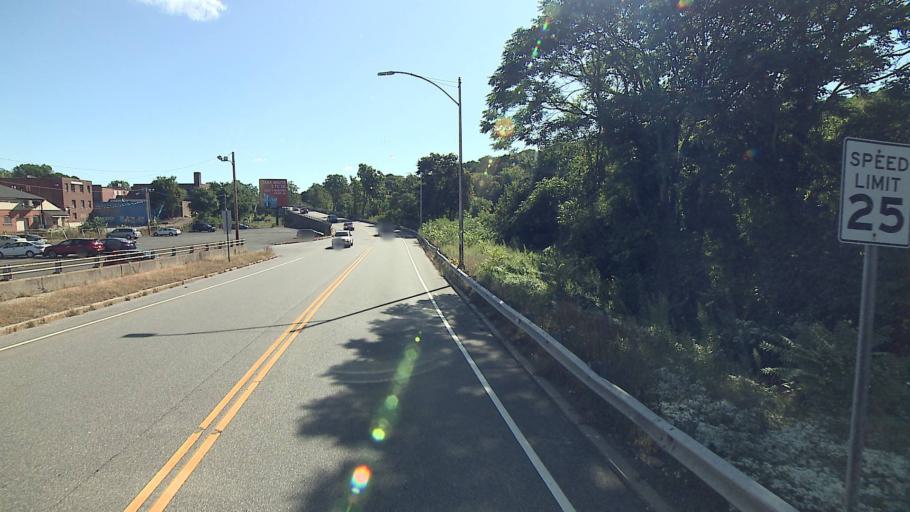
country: US
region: Connecticut
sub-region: New London County
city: Norwich
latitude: 41.5231
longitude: -72.0734
